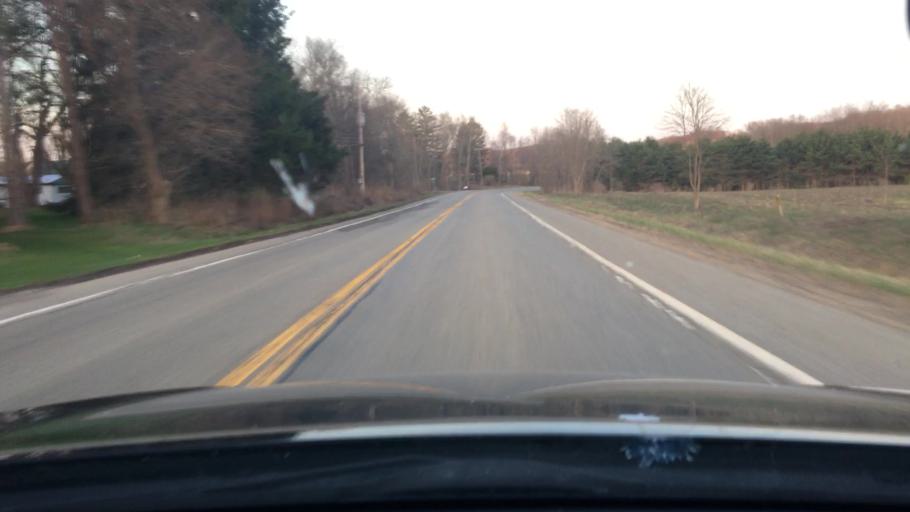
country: US
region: New York
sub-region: Cattaraugus County
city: Randolph
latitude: 42.1957
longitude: -78.9003
